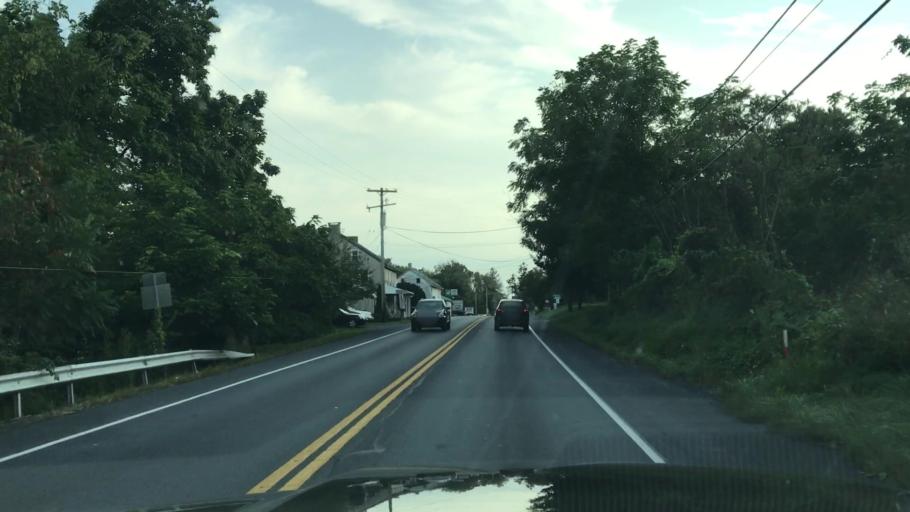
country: US
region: Pennsylvania
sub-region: Berks County
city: Bally
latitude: 40.4184
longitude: -75.5732
